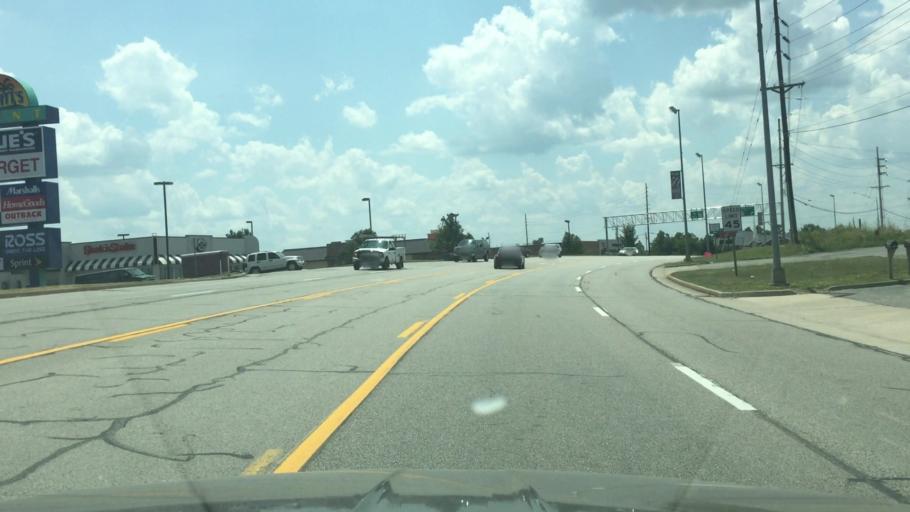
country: US
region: Missouri
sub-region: Miller County
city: Lake Ozark
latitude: 38.1592
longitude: -92.6055
